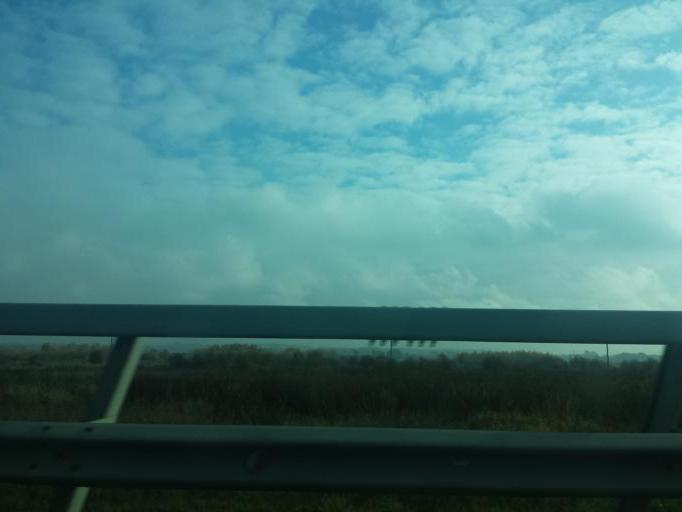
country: RU
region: Kaliningrad
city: Gur'yevsk
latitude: 54.7817
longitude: 20.5450
